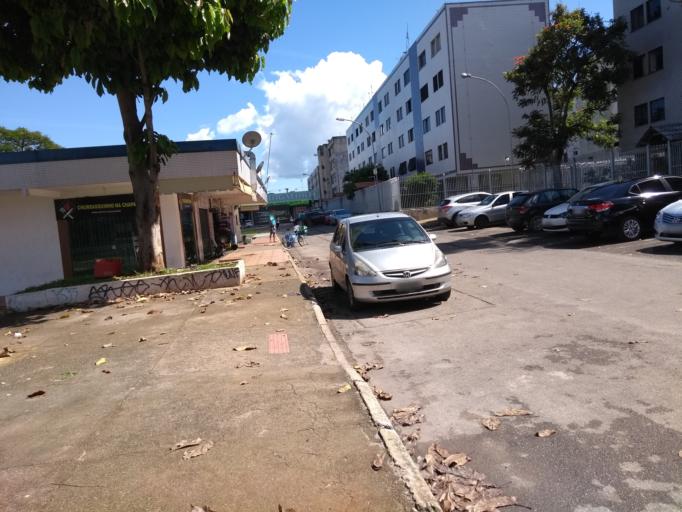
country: BR
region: Federal District
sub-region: Brasilia
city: Brasilia
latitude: -15.7989
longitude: -47.9411
